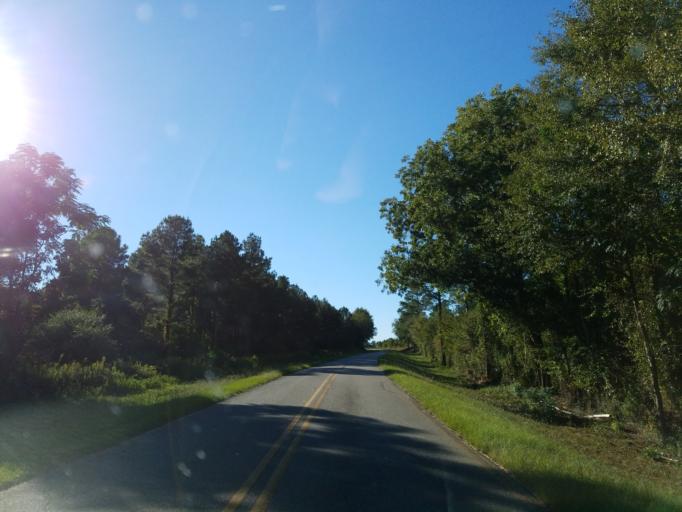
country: US
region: Georgia
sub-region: Lee County
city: Leesburg
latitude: 31.9120
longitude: -84.0288
